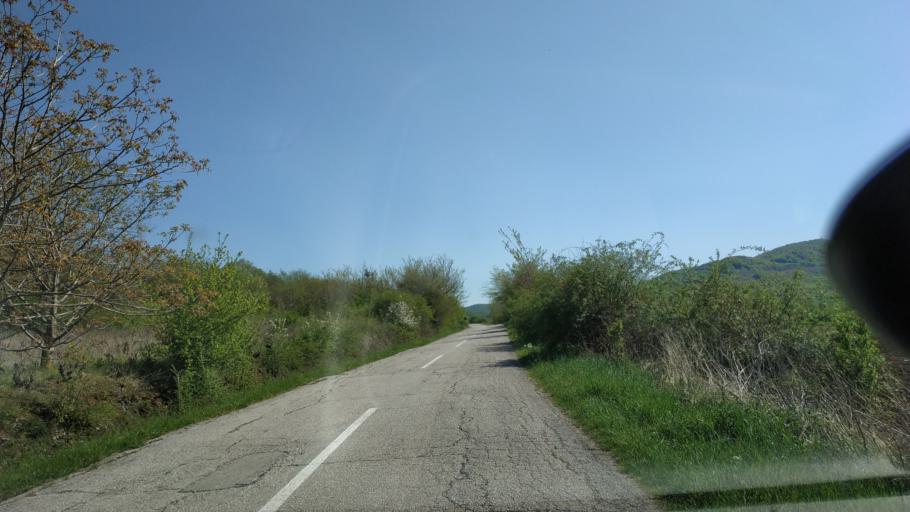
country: RS
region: Central Serbia
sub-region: Nisavski Okrug
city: Nis
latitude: 43.4361
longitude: 21.8467
